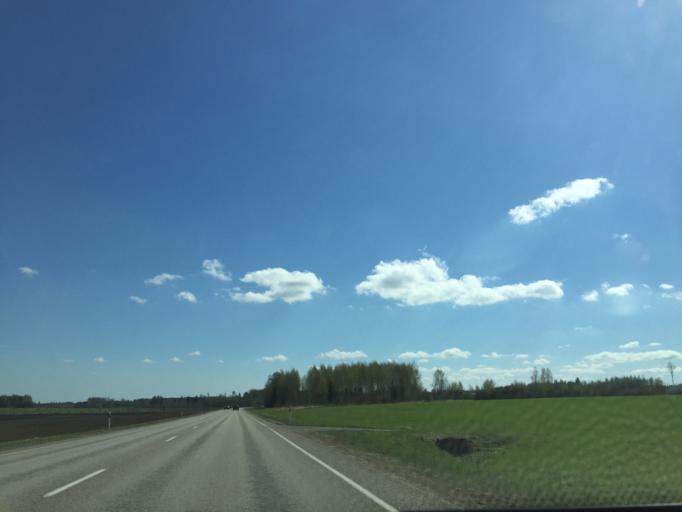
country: EE
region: Valgamaa
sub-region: Valga linn
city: Valga
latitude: 57.8792
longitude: 26.0598
